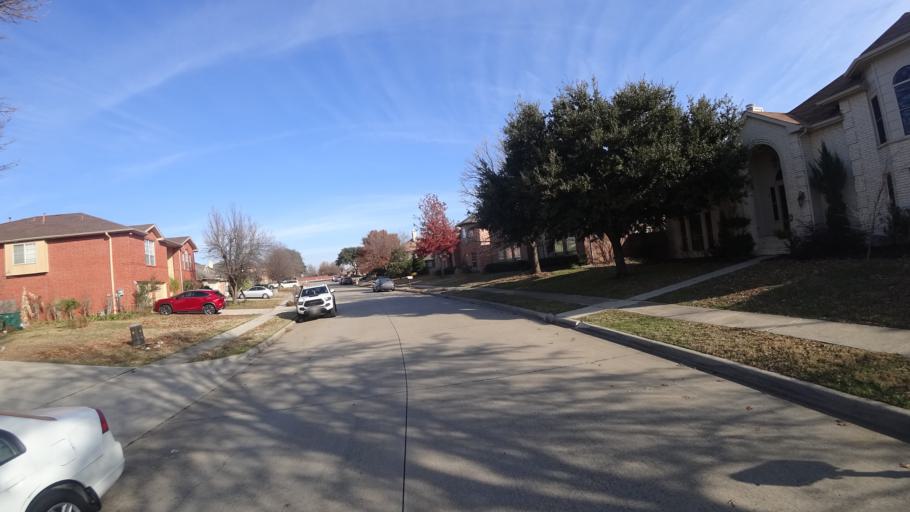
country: US
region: Texas
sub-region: Denton County
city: Lewisville
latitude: 33.0556
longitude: -97.0219
